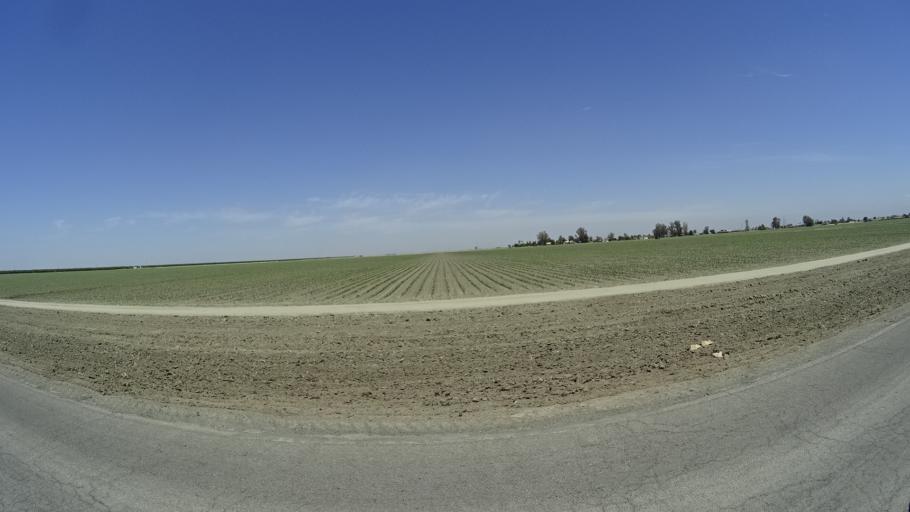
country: US
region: California
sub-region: Kings County
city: Corcoran
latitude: 36.1090
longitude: -119.5831
